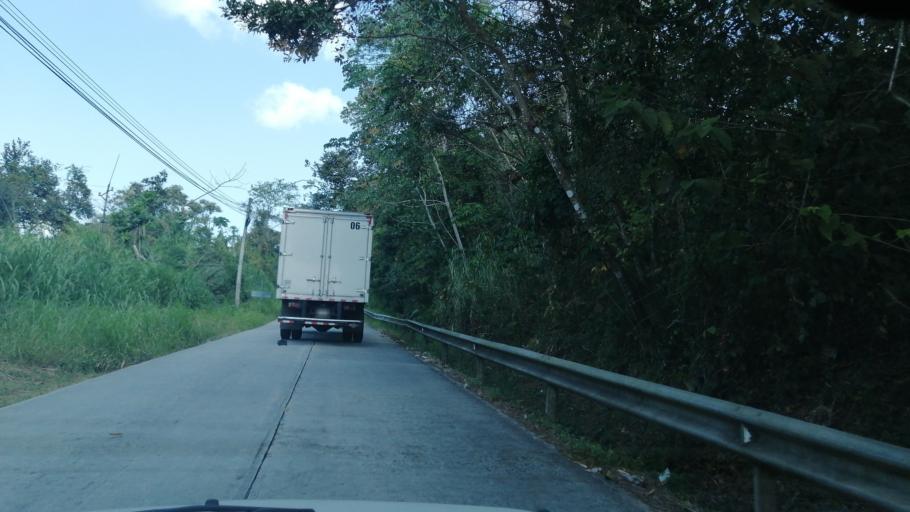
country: PA
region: Panama
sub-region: Distrito de Panama
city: Ancon
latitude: 8.9363
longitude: -79.5739
